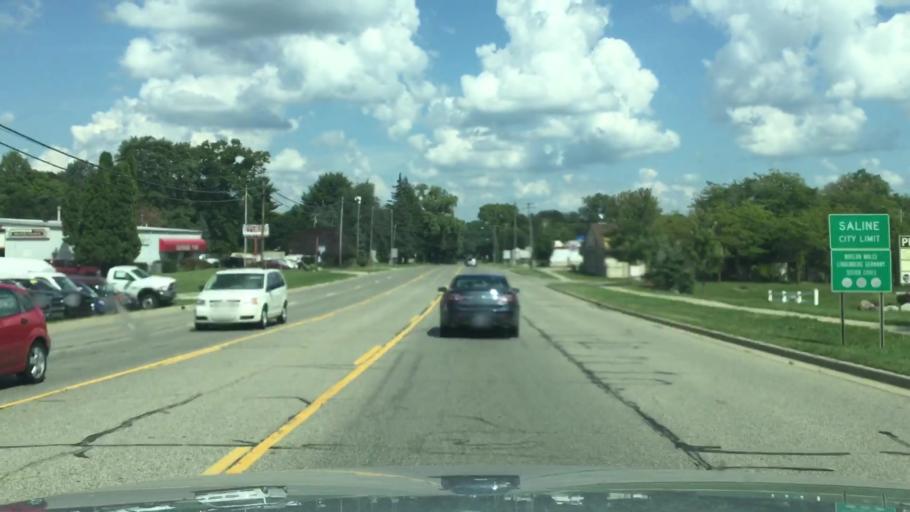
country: US
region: Michigan
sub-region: Washtenaw County
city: Saline
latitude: 42.1608
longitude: -83.7960
